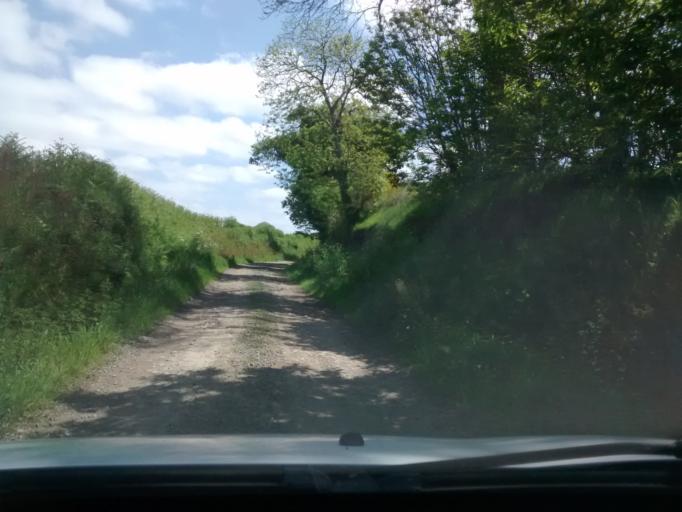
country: FR
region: Brittany
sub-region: Departement des Cotes-d'Armor
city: Louannec
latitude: 48.7858
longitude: -3.4106
